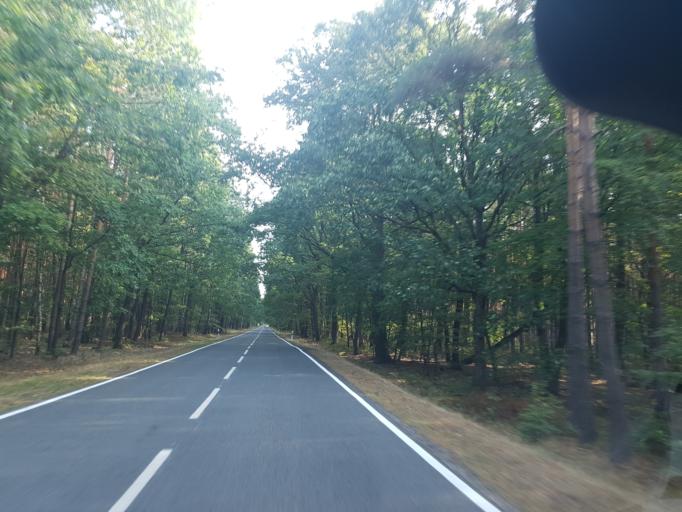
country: DE
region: Brandenburg
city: Wiesenburg
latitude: 52.0769
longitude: 12.4069
